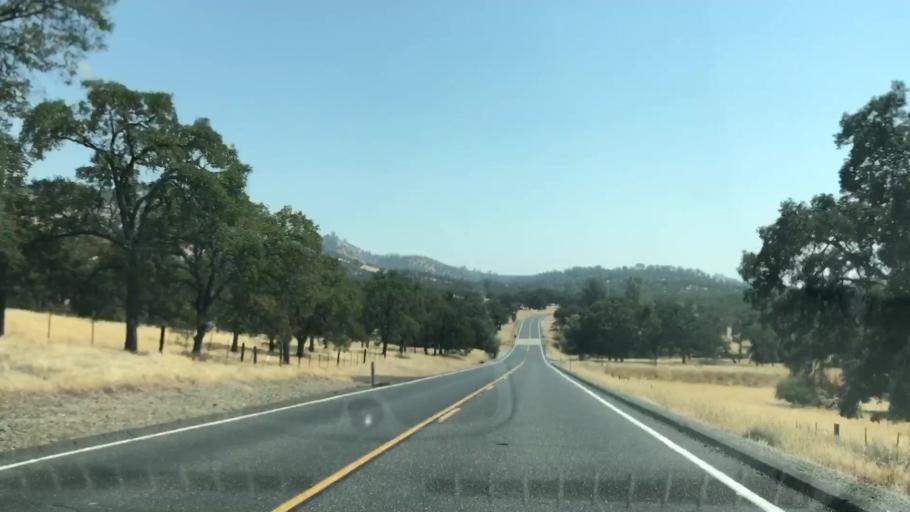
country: US
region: California
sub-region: Calaveras County
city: Copperopolis
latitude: 37.9629
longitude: -120.6173
